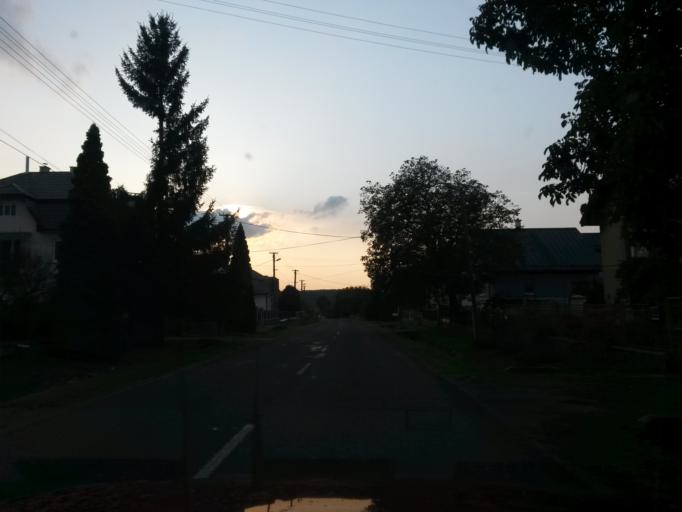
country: SK
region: Kosicky
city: Kosice
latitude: 48.7668
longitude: 21.4379
